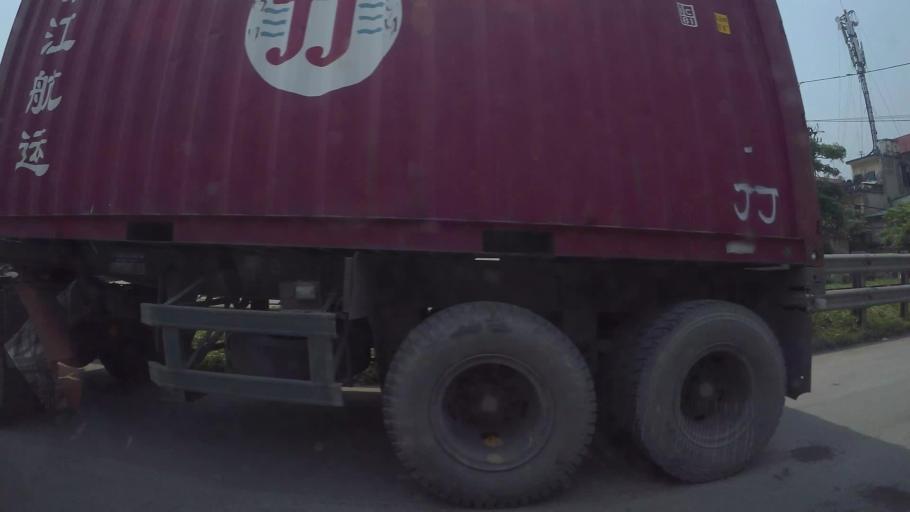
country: VN
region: Ha Noi
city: Van Dien
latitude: 20.9499
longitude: 105.8442
